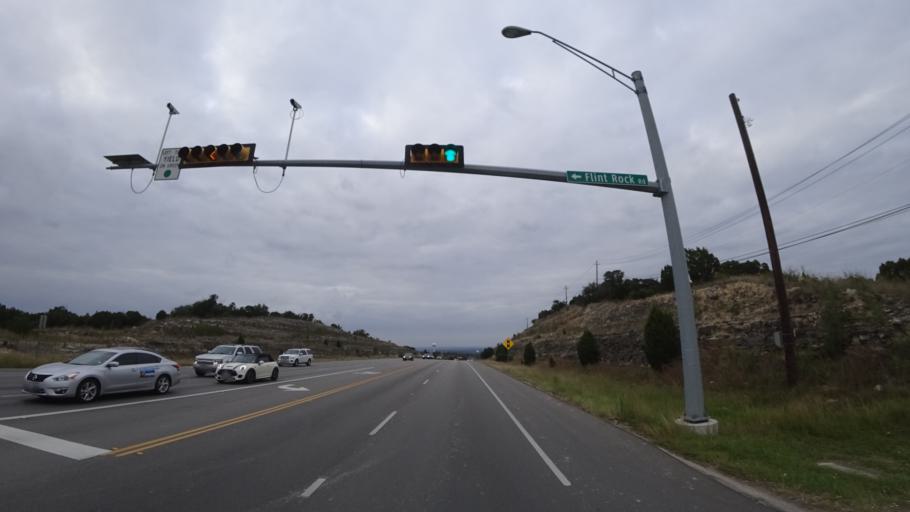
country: US
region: Texas
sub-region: Travis County
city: The Hills
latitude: 30.3346
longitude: -97.9688
